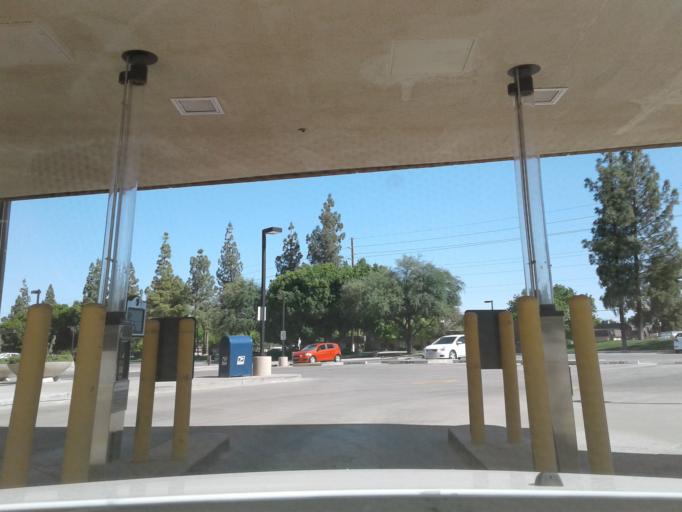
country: US
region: Arizona
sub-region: Maricopa County
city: Tempe
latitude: 33.3937
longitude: -111.9161
